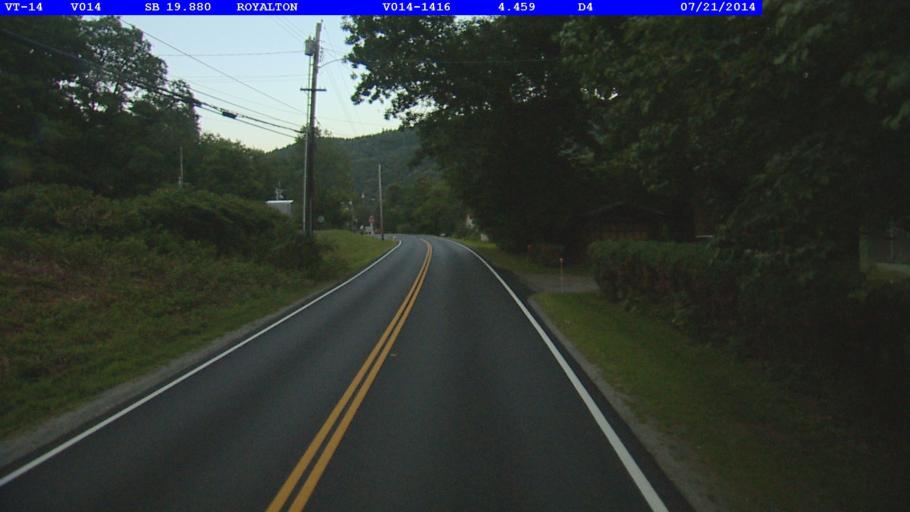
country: US
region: Vermont
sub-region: Orange County
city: Randolph
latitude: 43.8146
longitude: -72.5498
